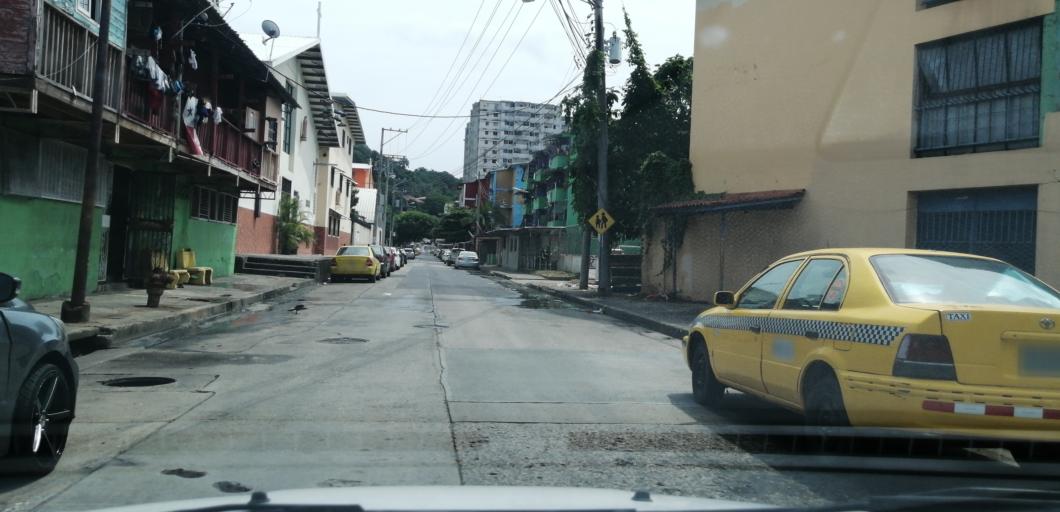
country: PA
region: Panama
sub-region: Distrito de Panama
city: Ancon
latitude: 8.9478
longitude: -79.5481
